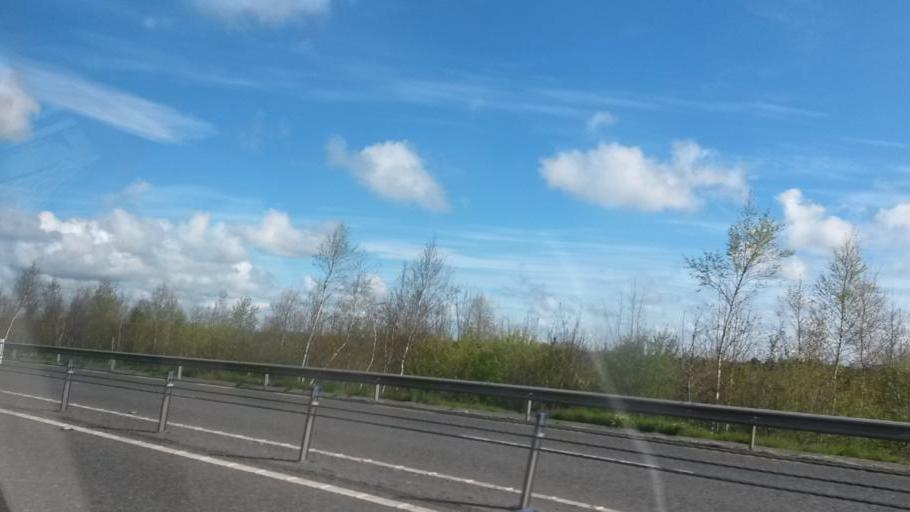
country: IE
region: Ulster
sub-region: An Cabhan
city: Mullagh
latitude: 53.7389
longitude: -6.9681
